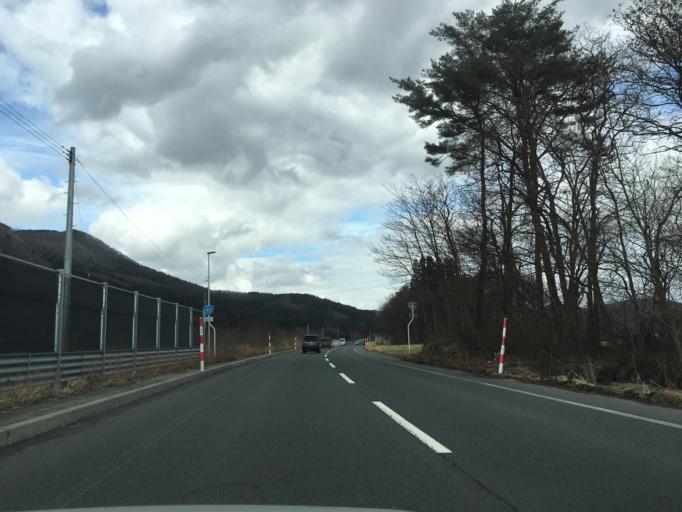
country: JP
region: Akita
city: Hanawa
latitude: 40.2294
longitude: 140.6810
